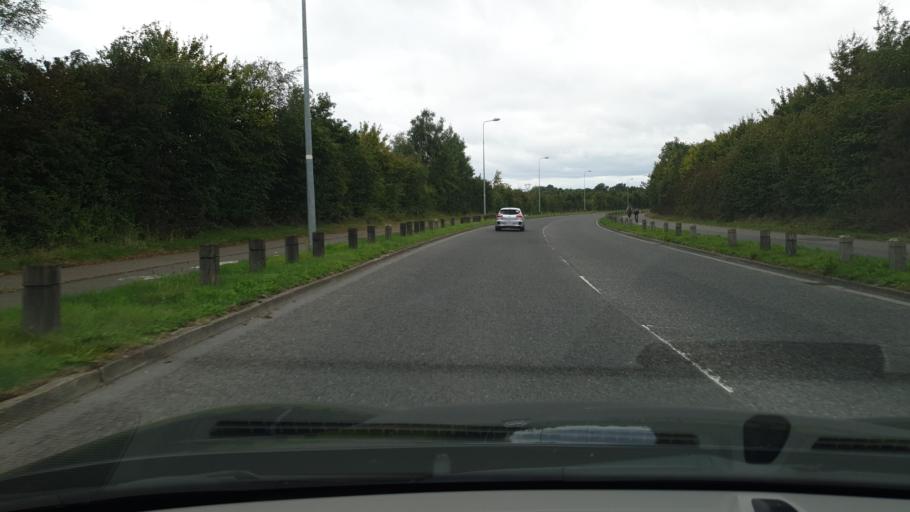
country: IE
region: Leinster
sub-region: Kildare
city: Naas
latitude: 53.2192
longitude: -6.6894
